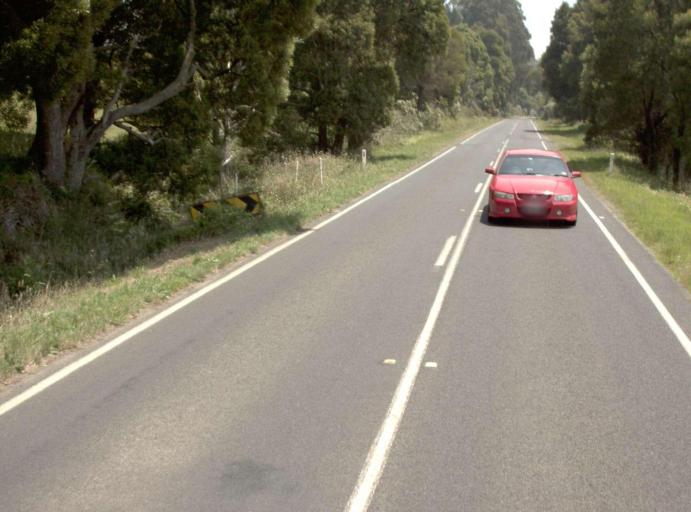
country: AU
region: Victoria
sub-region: Latrobe
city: Traralgon
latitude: -38.3553
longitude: 146.7182
